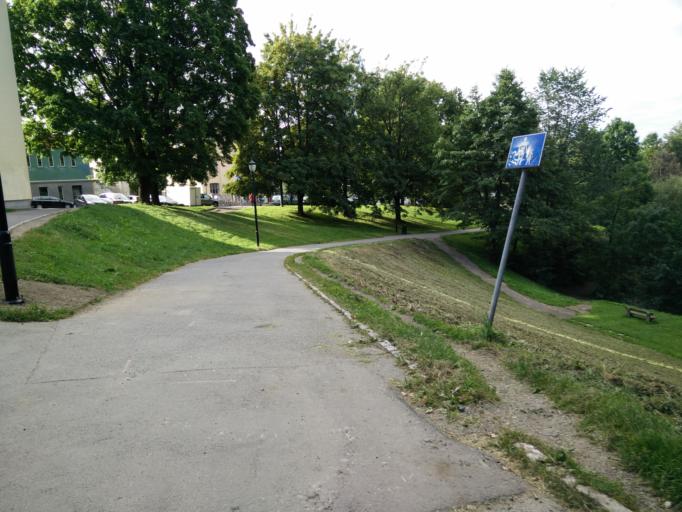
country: NO
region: Oslo
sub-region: Oslo
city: Oslo
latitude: 59.9320
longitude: 10.7584
